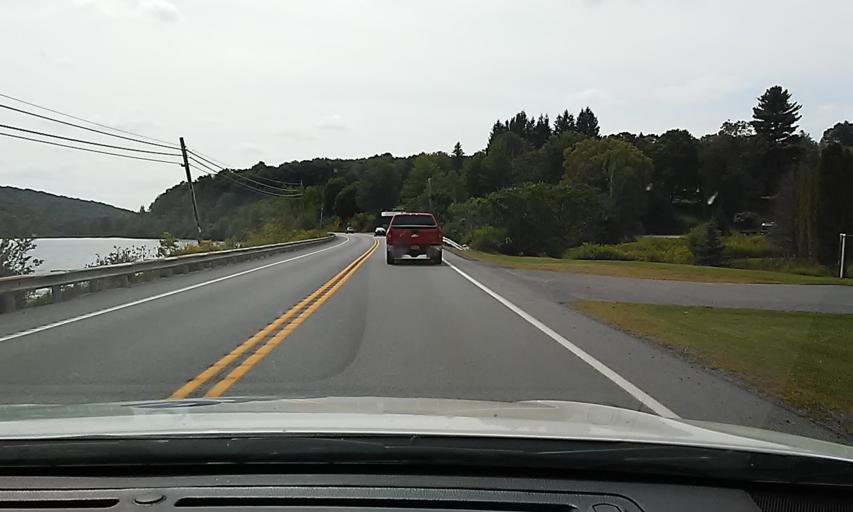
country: US
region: Pennsylvania
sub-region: Clearfield County
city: Treasure Lake
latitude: 41.1601
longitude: -78.6668
